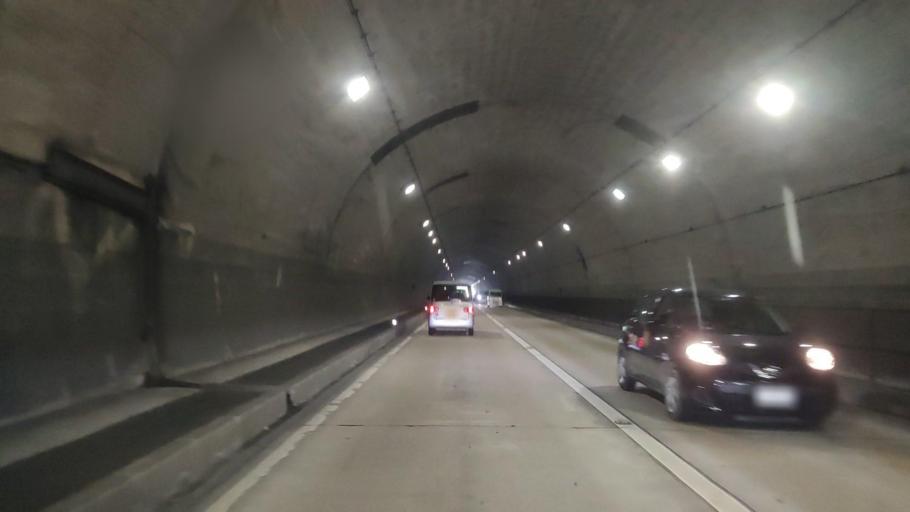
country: JP
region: Wakayama
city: Tanabe
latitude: 33.7139
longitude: 135.4502
